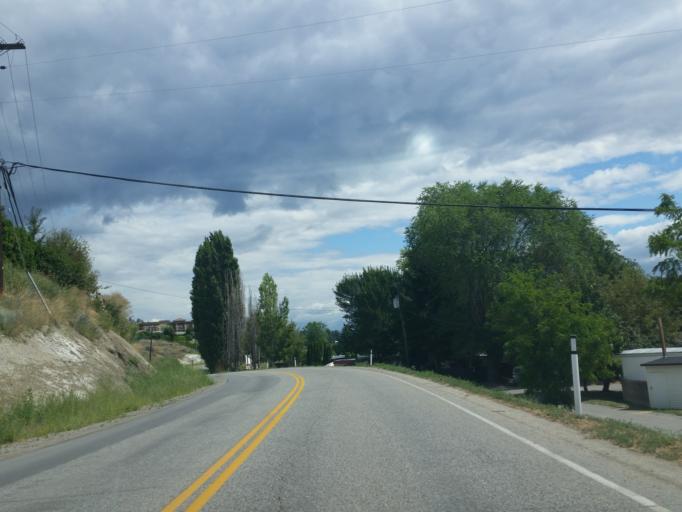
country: CA
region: British Columbia
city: West Kelowna
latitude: 49.8257
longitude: -119.6065
